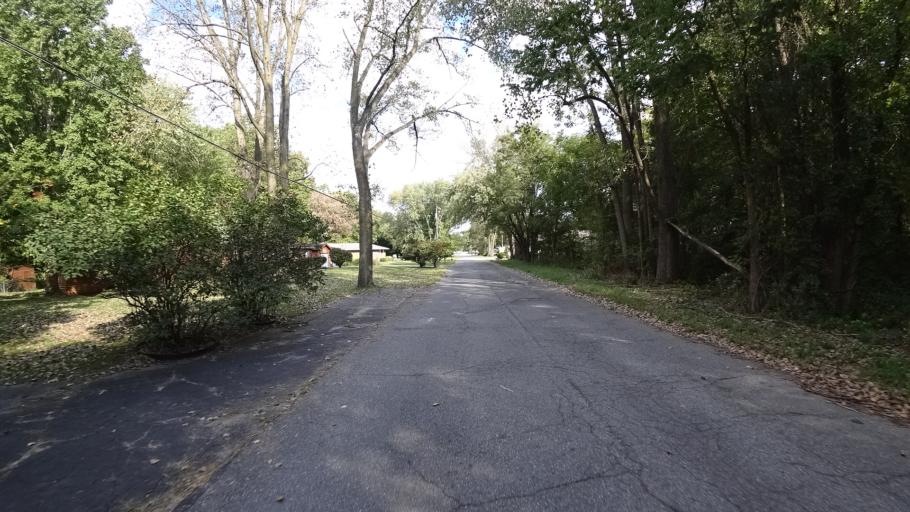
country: US
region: Indiana
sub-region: LaPorte County
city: Trail Creek
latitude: 41.6923
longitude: -86.8714
